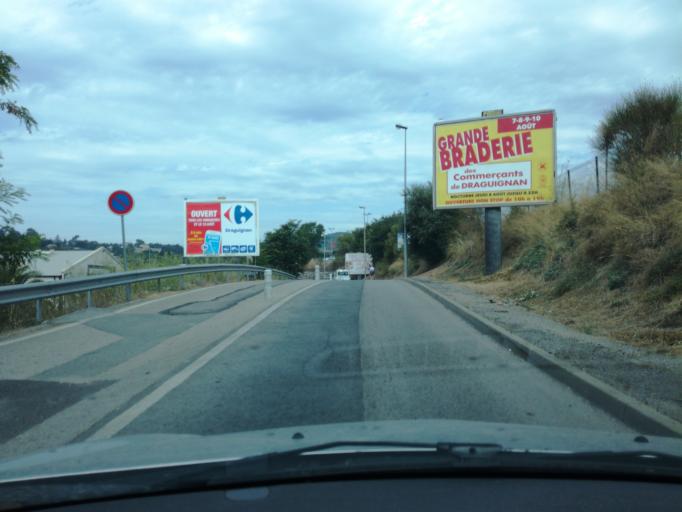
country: FR
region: Provence-Alpes-Cote d'Azur
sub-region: Departement du Var
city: Draguignan
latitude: 43.5269
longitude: 6.4537
